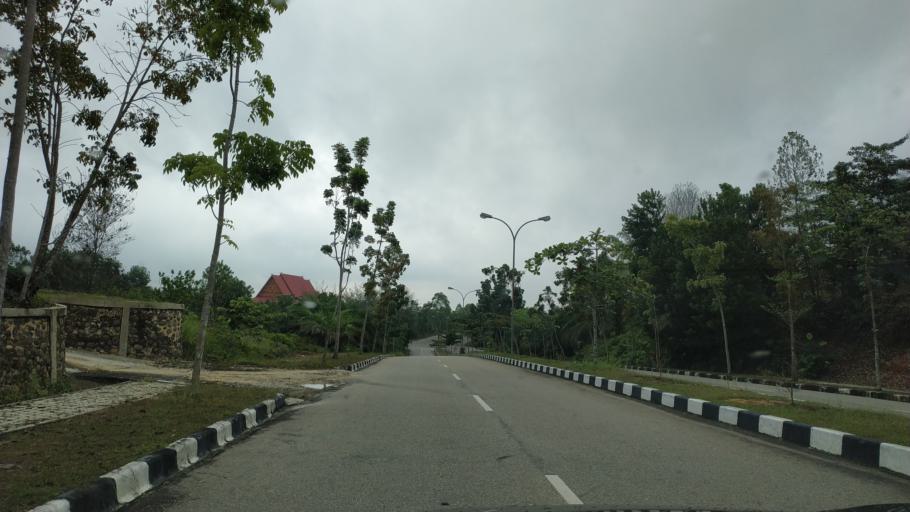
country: ID
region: Riau
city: Pangkalanbunut
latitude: 0.3805
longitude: 101.8273
